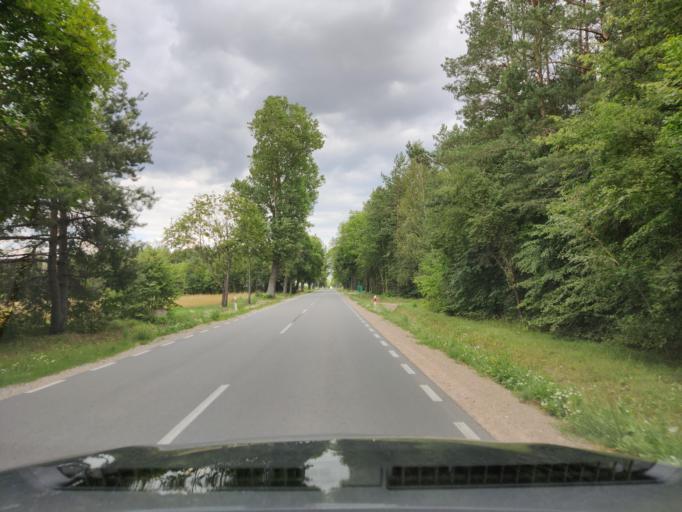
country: PL
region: Masovian Voivodeship
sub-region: Powiat sokolowski
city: Kosow Lacki
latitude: 52.6030
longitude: 22.1788
